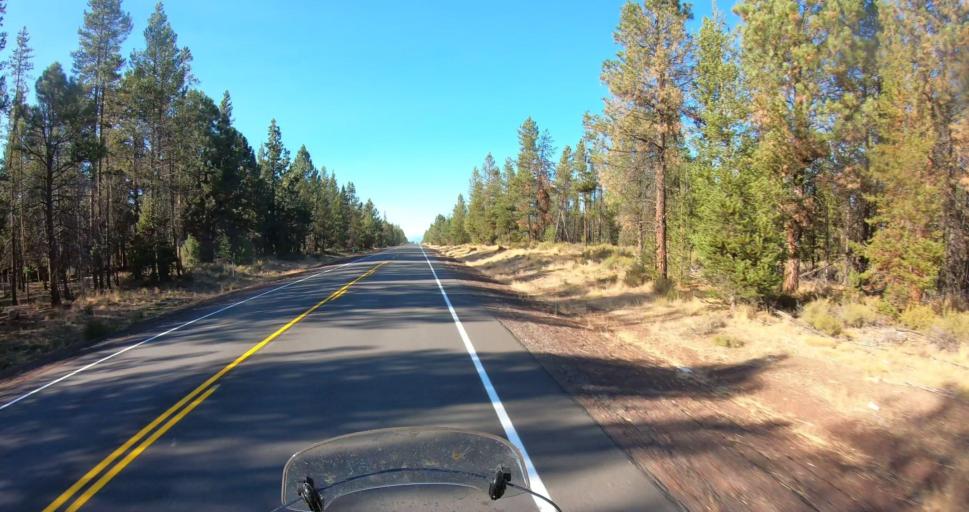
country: US
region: Oregon
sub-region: Deschutes County
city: La Pine
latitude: 43.5388
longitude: -121.4653
